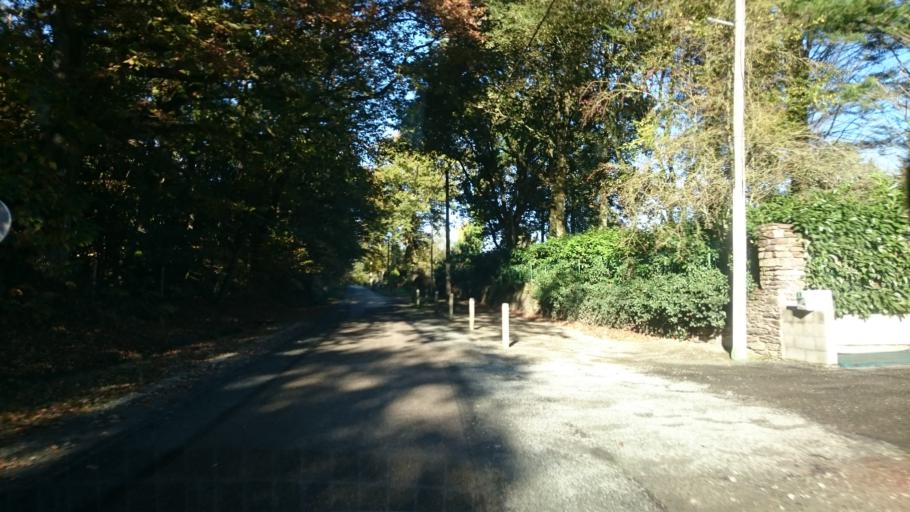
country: FR
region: Brittany
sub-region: Departement d'Ille-et-Vilaine
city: Laille
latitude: 47.9697
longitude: -1.7091
